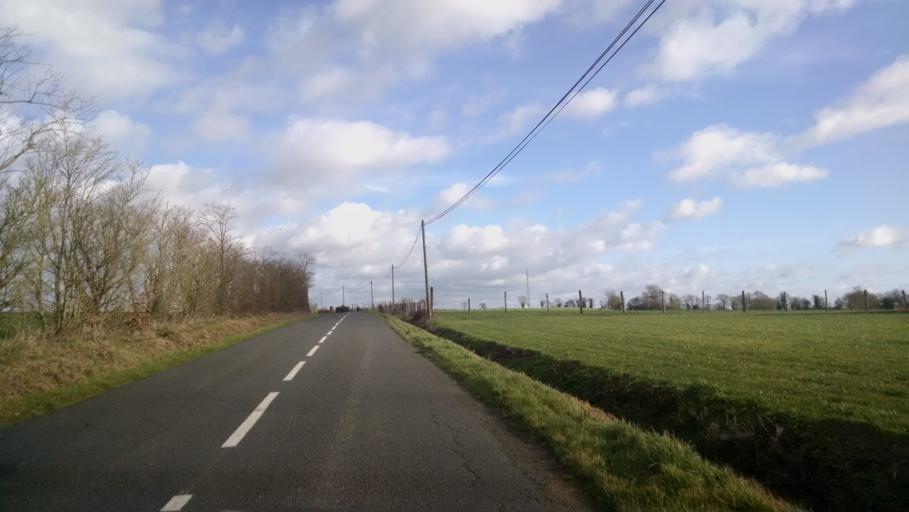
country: FR
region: Pays de la Loire
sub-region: Departement de la Loire-Atlantique
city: Remouille
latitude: 47.0581
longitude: -1.3593
